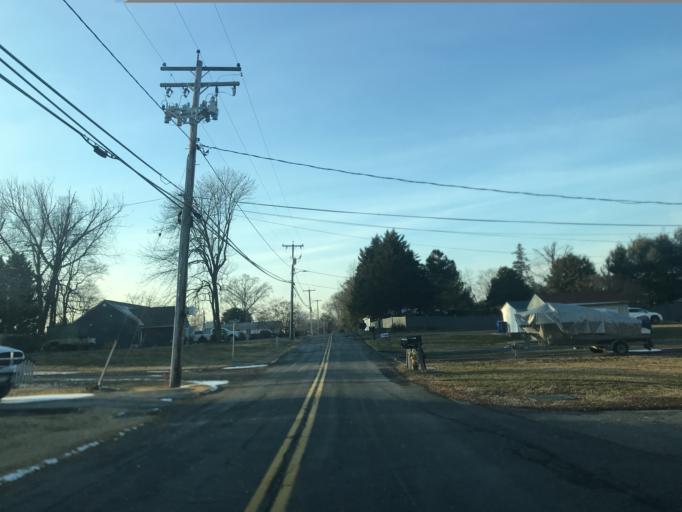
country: US
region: Maryland
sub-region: Harford County
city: Riverside
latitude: 39.4397
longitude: -76.2527
